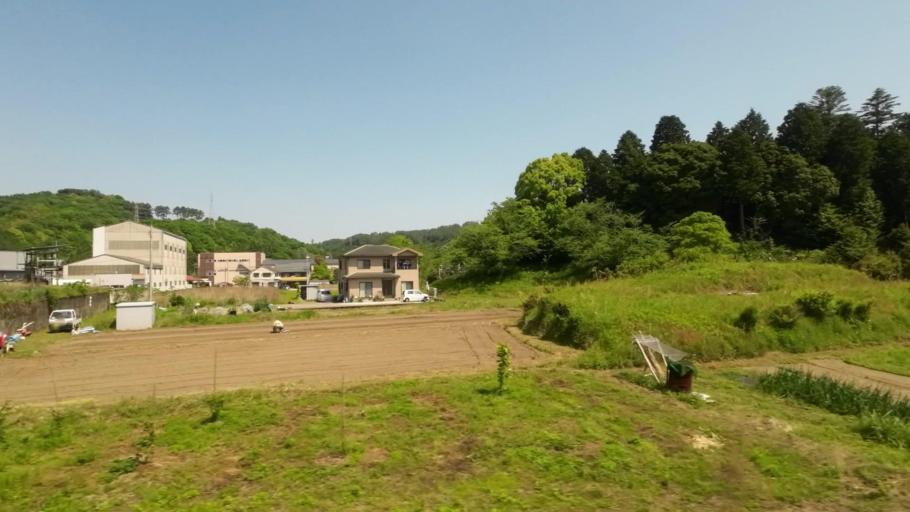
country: JP
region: Ehime
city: Niihama
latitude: 33.9279
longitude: 133.2627
